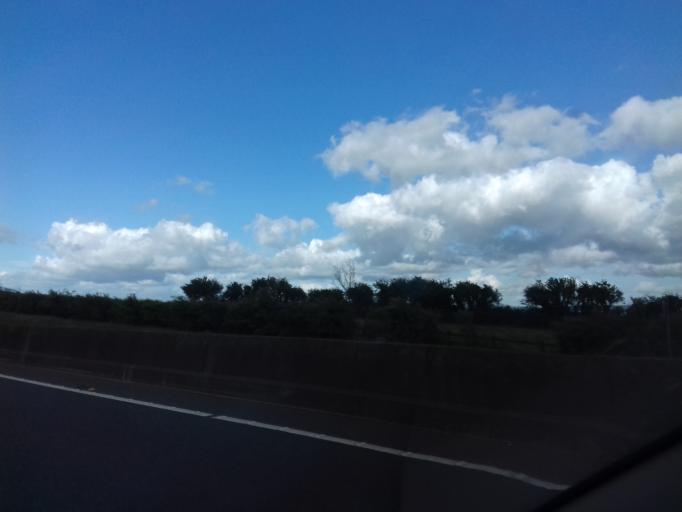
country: IE
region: Leinster
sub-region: Kilkenny
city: Kilkenny
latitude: 52.5526
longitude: -7.2479
